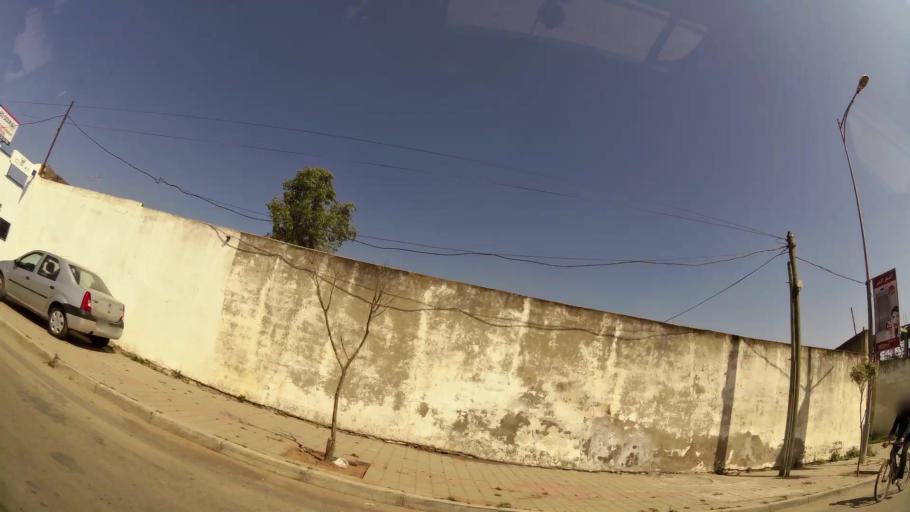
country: MA
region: Rabat-Sale-Zemmour-Zaer
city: Sale
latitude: 34.0758
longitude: -6.7543
